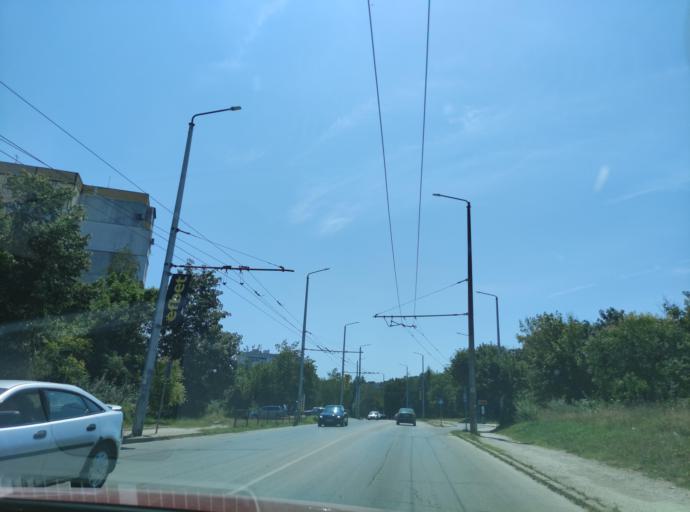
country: BG
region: Pleven
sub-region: Obshtina Pleven
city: Pleven
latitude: 43.4253
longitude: 24.5907
